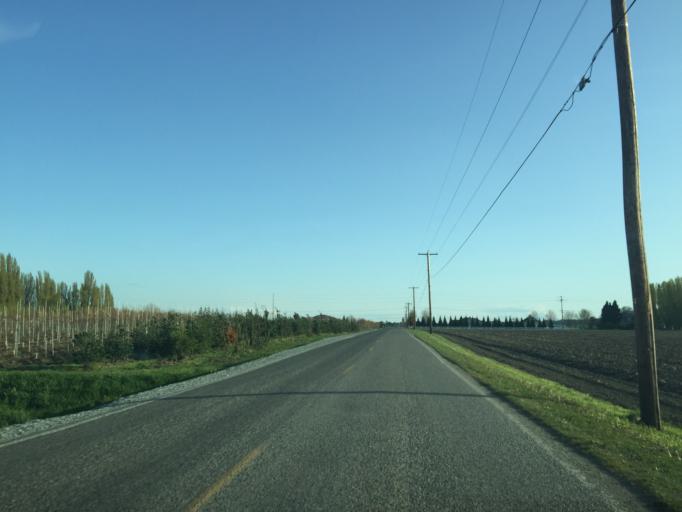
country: US
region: Washington
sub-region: Skagit County
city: Mount Vernon
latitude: 48.4237
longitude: -122.4221
